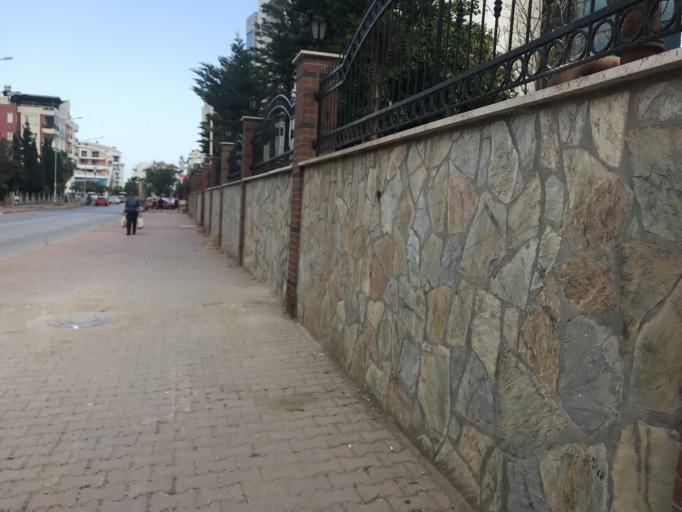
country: TR
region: Antalya
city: Cakirlar
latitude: 36.8496
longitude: 30.6117
